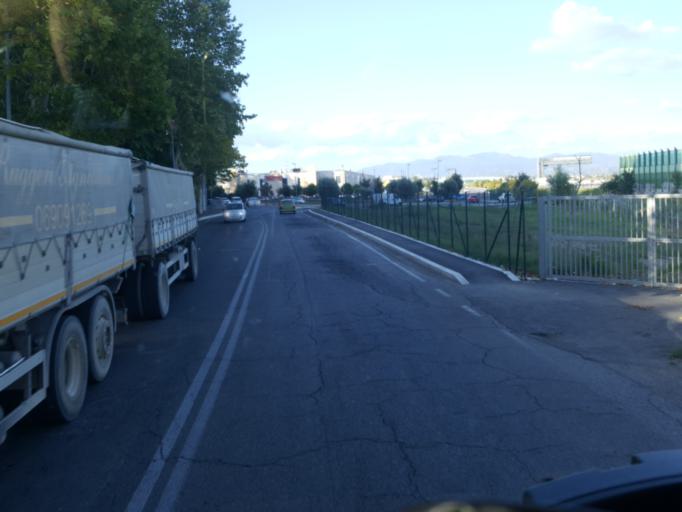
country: IT
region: Latium
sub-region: Citta metropolitana di Roma Capitale
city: Girardi-Bellavista-Terrazze
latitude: 42.1023
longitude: 12.5827
